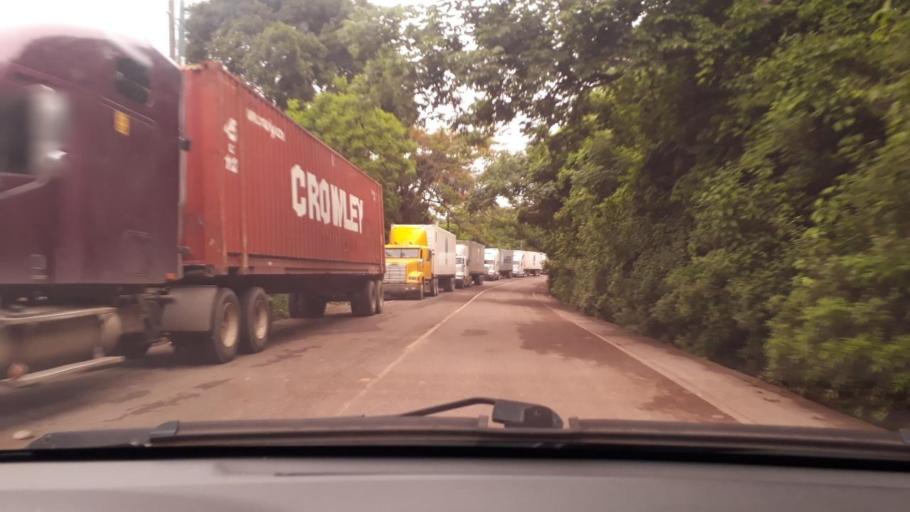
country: SV
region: Santa Ana
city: Metapan
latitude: 14.4204
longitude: -89.4443
